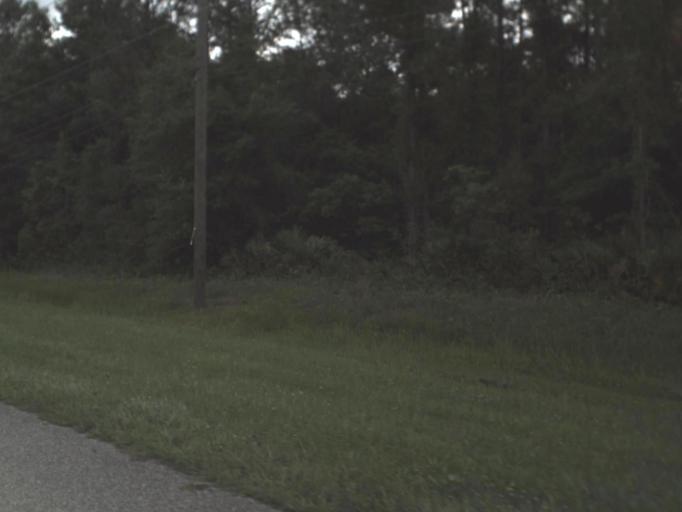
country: US
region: Florida
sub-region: Nassau County
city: Nassau Village-Ratliff
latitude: 30.4708
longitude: -81.7788
